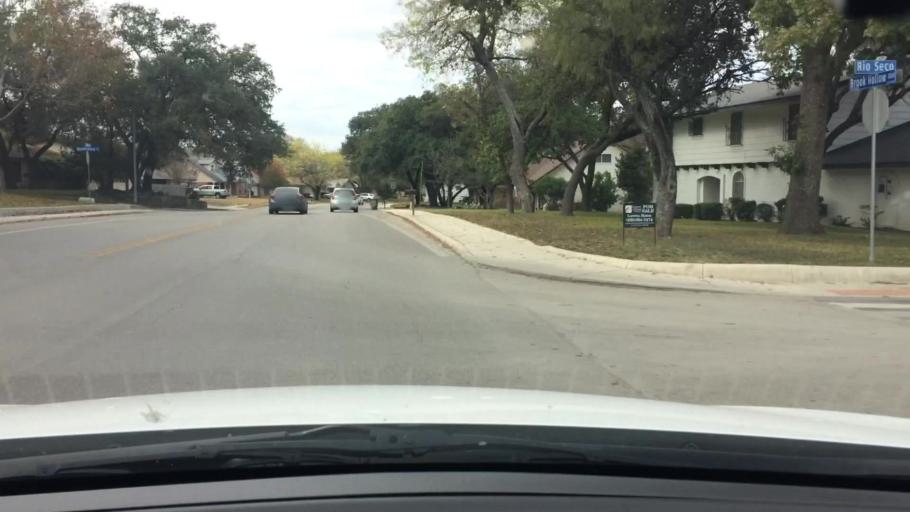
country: US
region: Texas
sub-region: Bexar County
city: Hollywood Park
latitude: 29.5762
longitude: -98.4687
